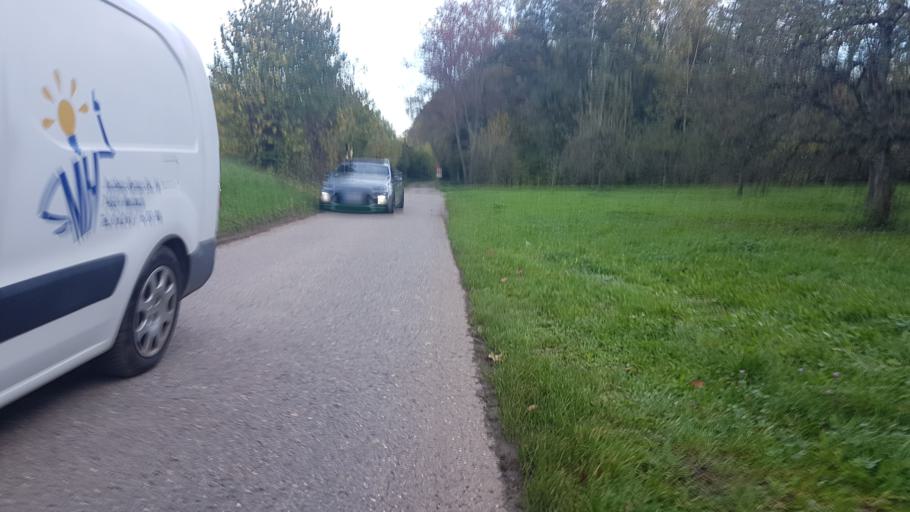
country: DE
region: Baden-Wuerttemberg
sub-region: Karlsruhe Region
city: Neckarzimmern
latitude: 49.3230
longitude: 9.1087
